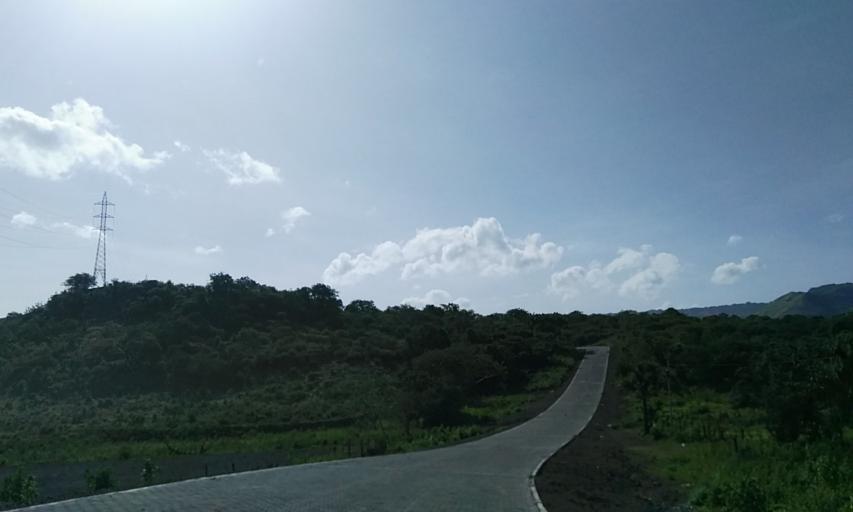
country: NI
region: Matagalpa
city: Terrabona
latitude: 12.7400
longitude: -86.0394
